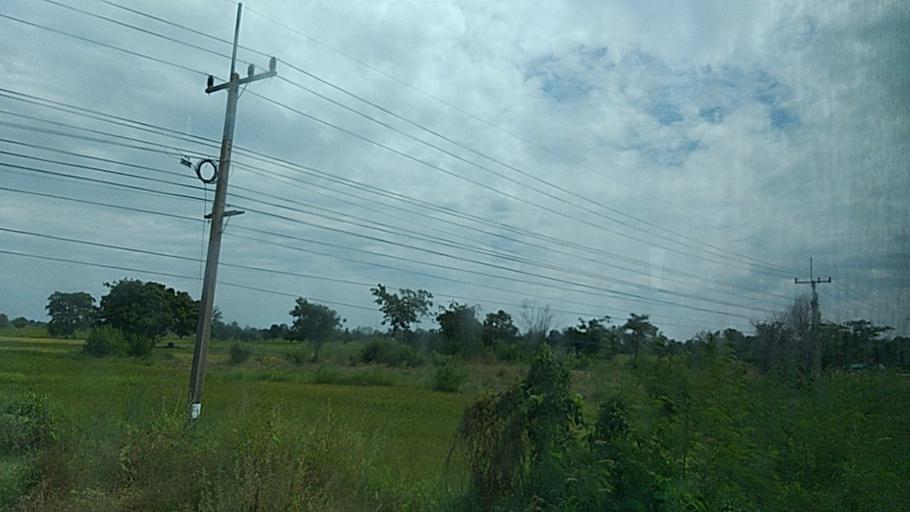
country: TH
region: Maha Sarakham
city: Chiang Yuen
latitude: 16.3576
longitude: 103.1135
